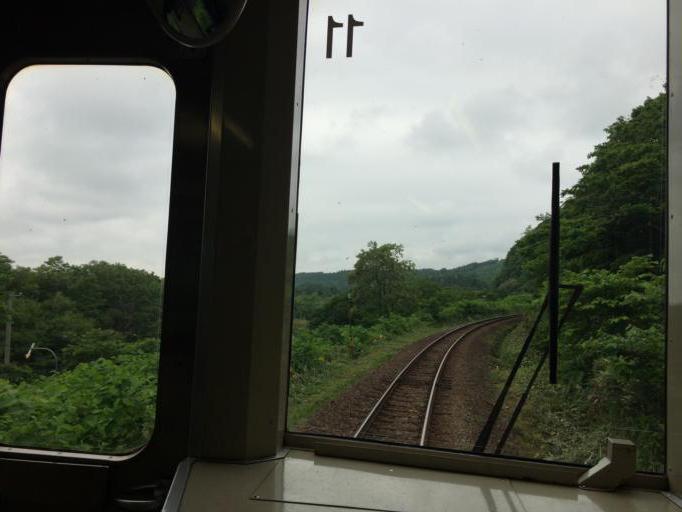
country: JP
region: Hokkaido
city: Iwanai
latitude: 42.9746
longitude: 140.6729
